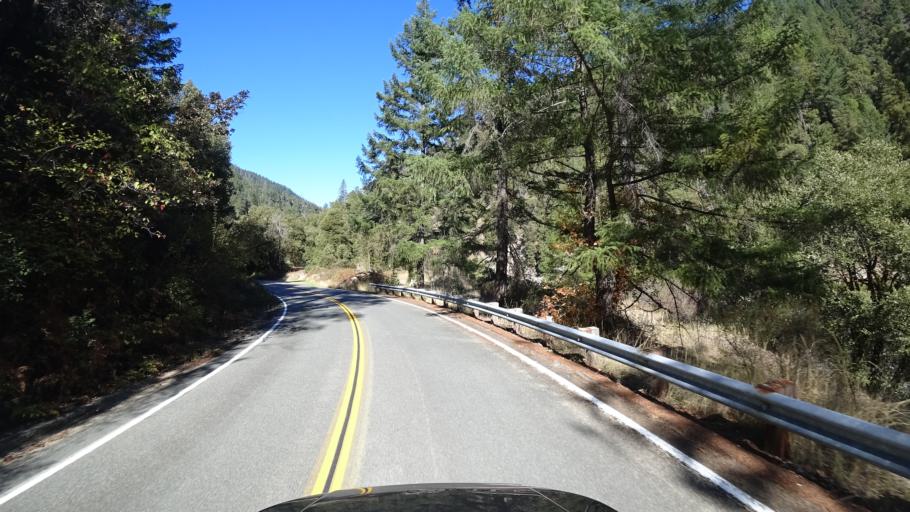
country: US
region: California
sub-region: Siskiyou County
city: Happy Camp
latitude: 41.3458
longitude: -123.4030
